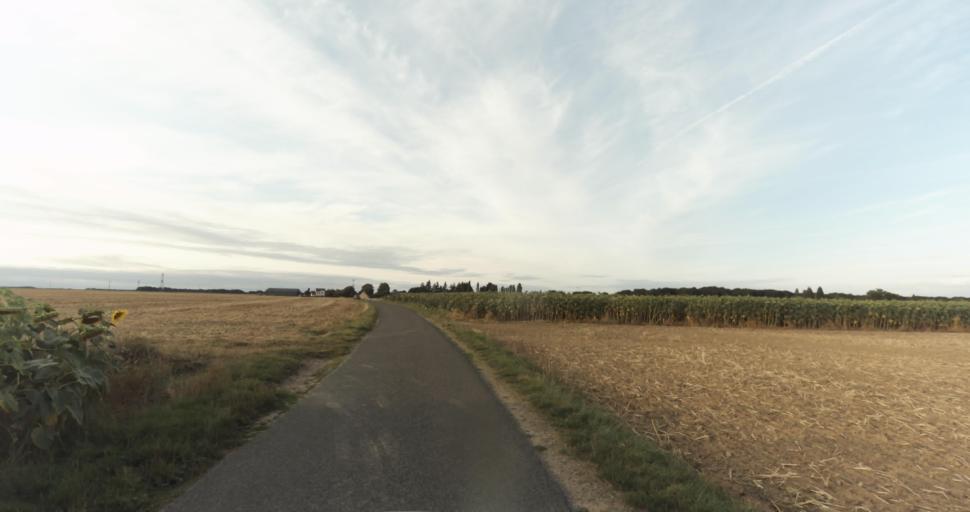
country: FR
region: Haute-Normandie
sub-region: Departement de l'Eure
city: Marcilly-sur-Eure
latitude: 48.8427
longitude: 1.2725
